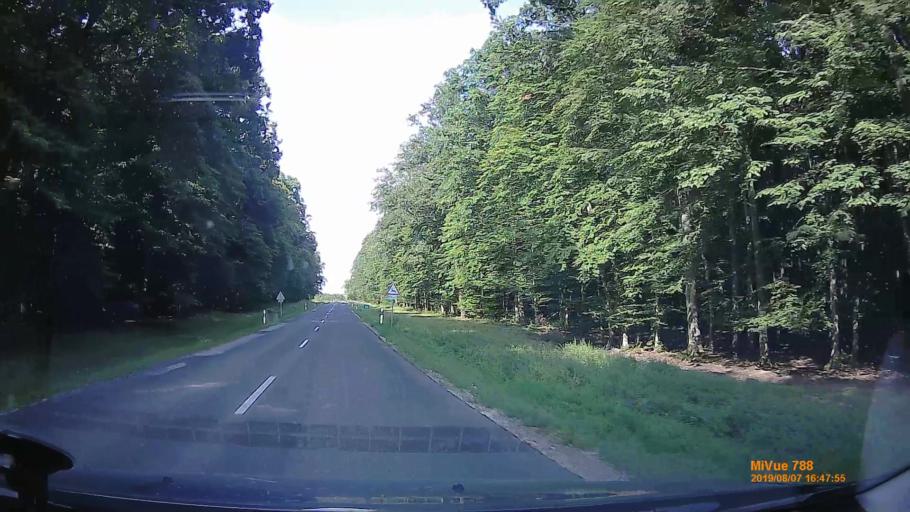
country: HU
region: Zala
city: Lenti
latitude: 46.6677
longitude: 16.6406
